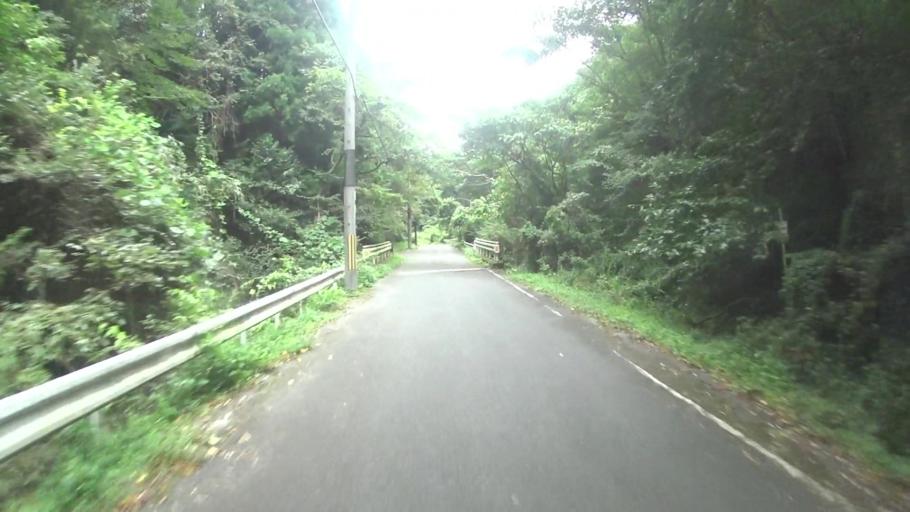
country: JP
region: Kyoto
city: Tanabe
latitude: 34.8108
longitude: 135.8598
